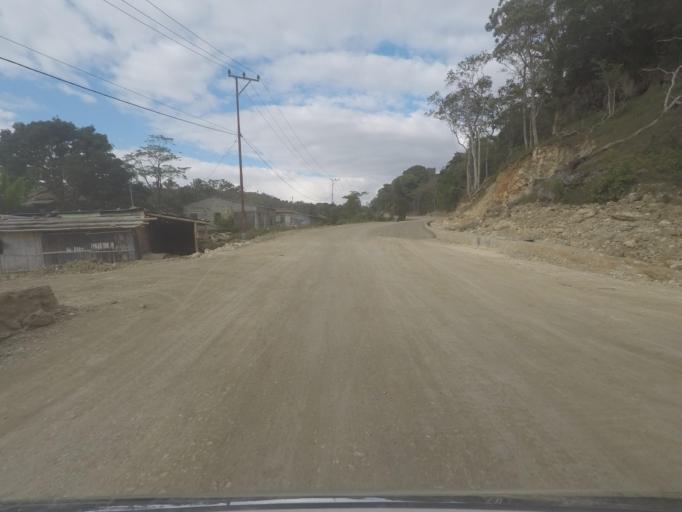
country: TL
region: Baucau
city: Venilale
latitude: -8.6300
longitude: 126.3825
